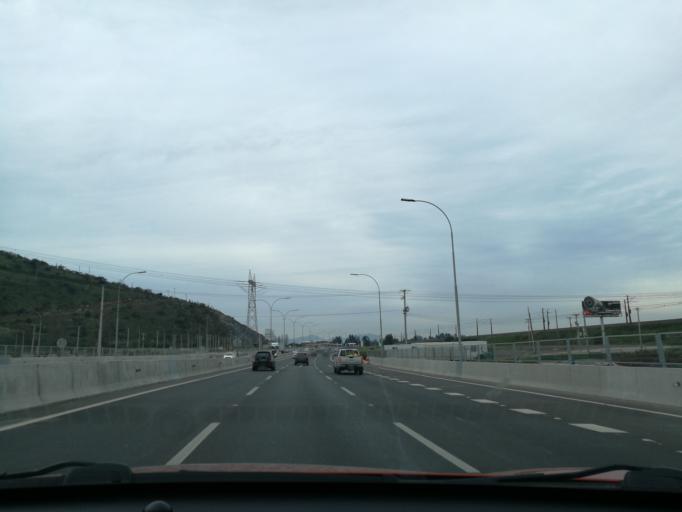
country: CL
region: Santiago Metropolitan
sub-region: Provincia de Maipo
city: Buin
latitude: -33.6875
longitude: -70.7260
